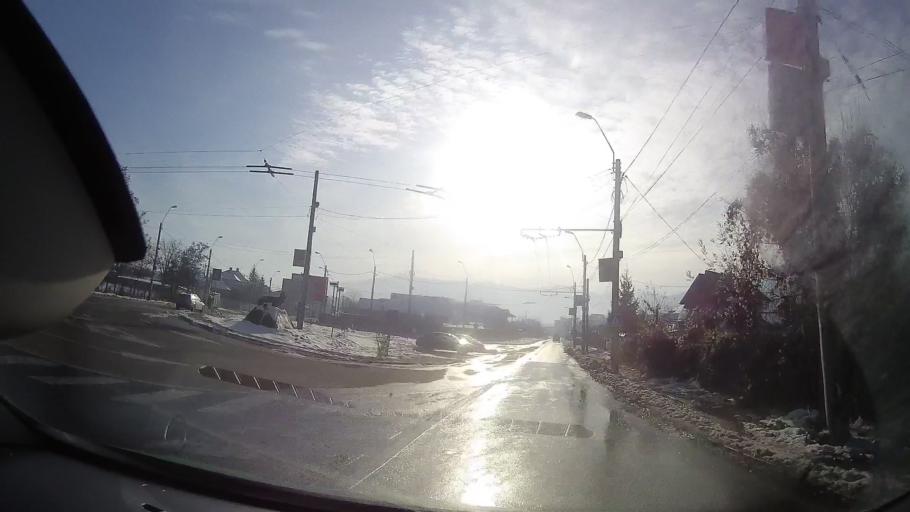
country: RO
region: Neamt
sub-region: Municipiul Piatra-Neamt
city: Valeni
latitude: 46.9473
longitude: 26.3849
